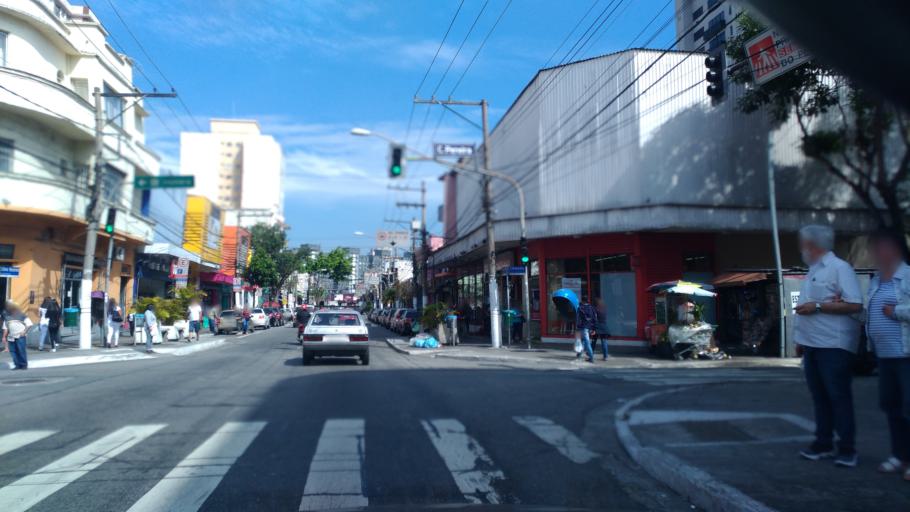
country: BR
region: Sao Paulo
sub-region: Sao Caetano Do Sul
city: Sao Caetano do Sul
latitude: -23.5979
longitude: -46.6007
